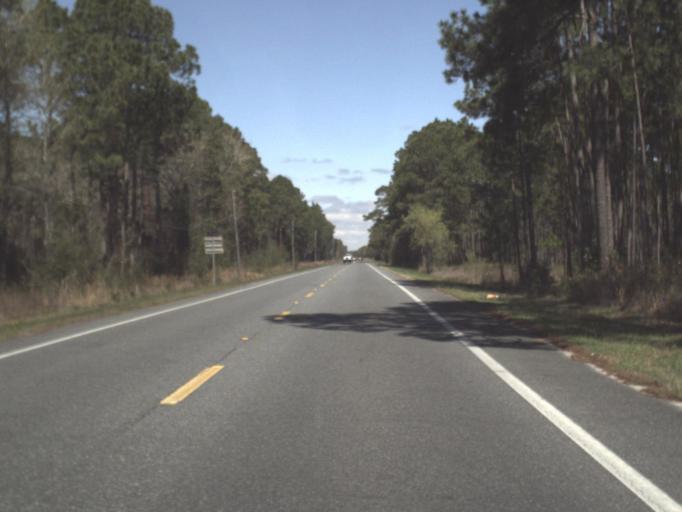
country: US
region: Florida
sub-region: Wakulla County
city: Crawfordville
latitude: 30.0467
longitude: -84.3880
